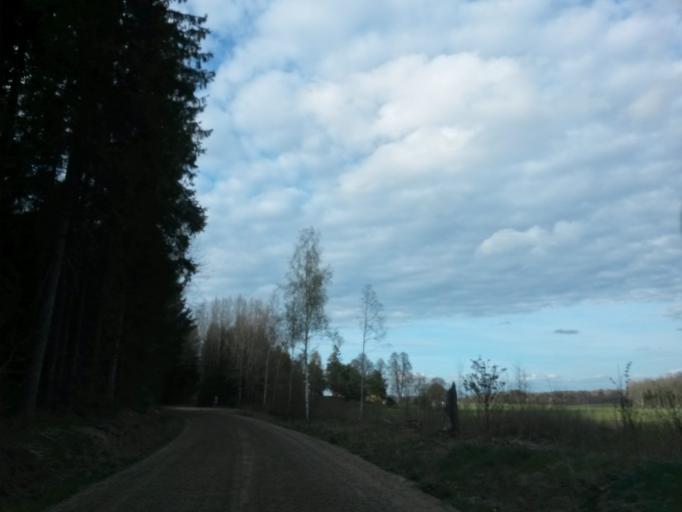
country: SE
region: Vaestra Goetaland
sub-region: Vargarda Kommun
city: Jonstorp
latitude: 58.0048
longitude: 12.6744
